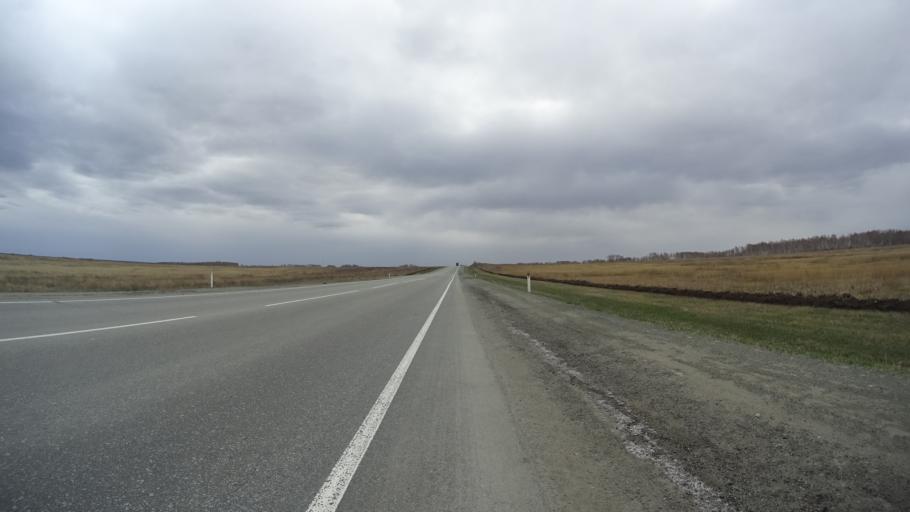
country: RU
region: Chelyabinsk
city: Yemanzhelinsk
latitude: 54.7100
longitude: 61.2595
